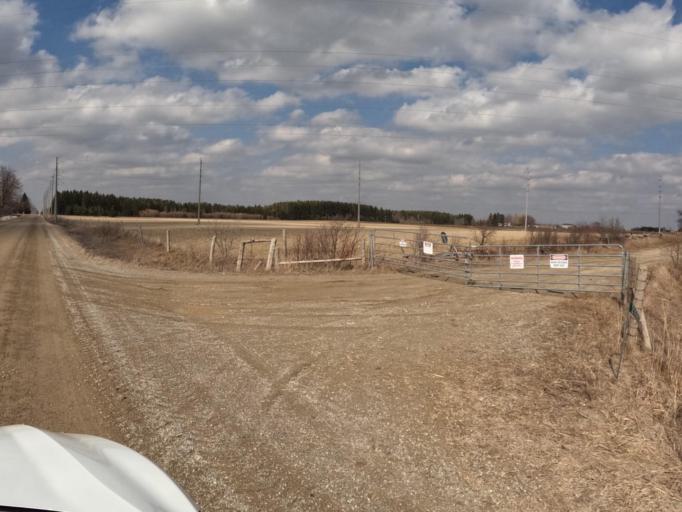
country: CA
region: Ontario
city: Shelburne
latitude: 43.9587
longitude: -80.2986
